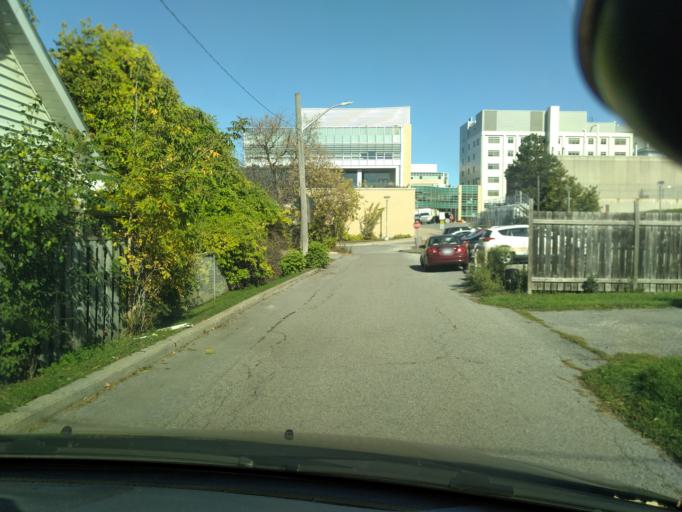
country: CA
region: Ontario
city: Newmarket
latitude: 44.0587
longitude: -79.4530
